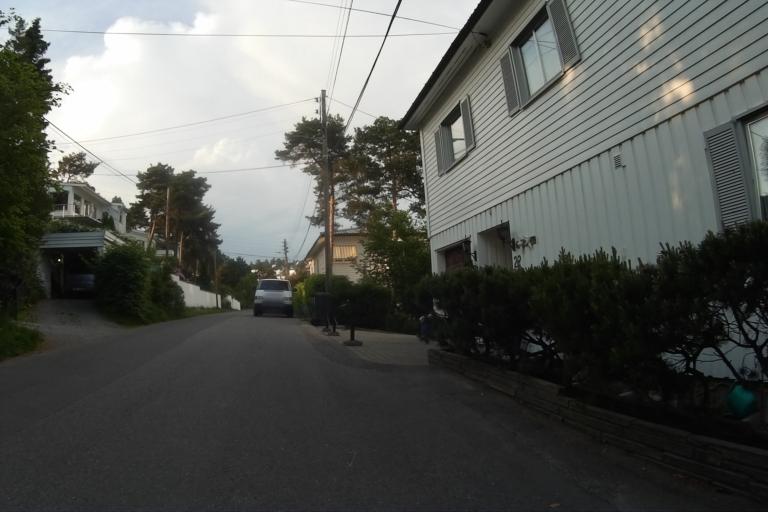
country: NO
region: Oslo
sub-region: Oslo
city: Oslo
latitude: 59.8676
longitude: 10.7740
